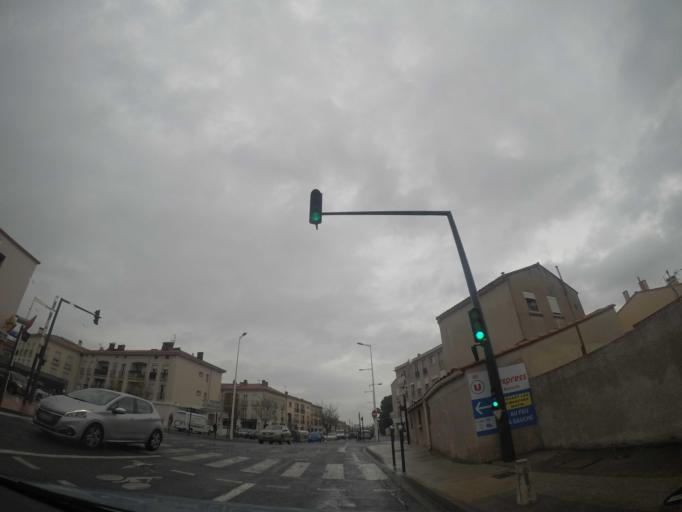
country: FR
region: Languedoc-Roussillon
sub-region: Departement des Pyrenees-Orientales
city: Perpignan
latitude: 42.6941
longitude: 2.8724
